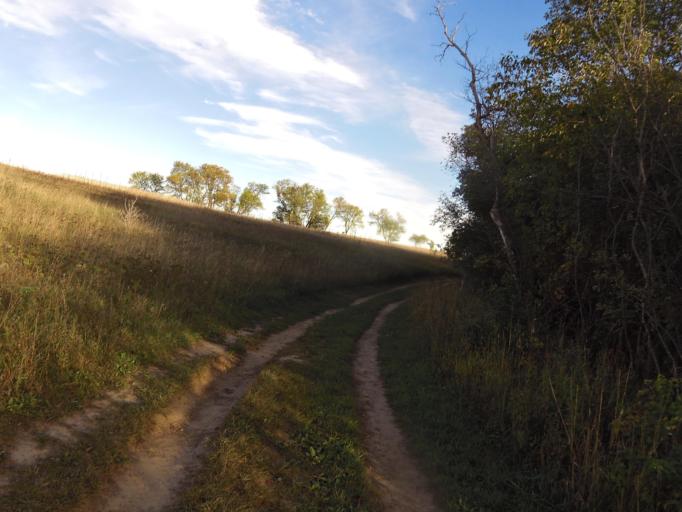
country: US
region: Minnesota
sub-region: Washington County
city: Afton
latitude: 44.8641
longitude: -92.7928
